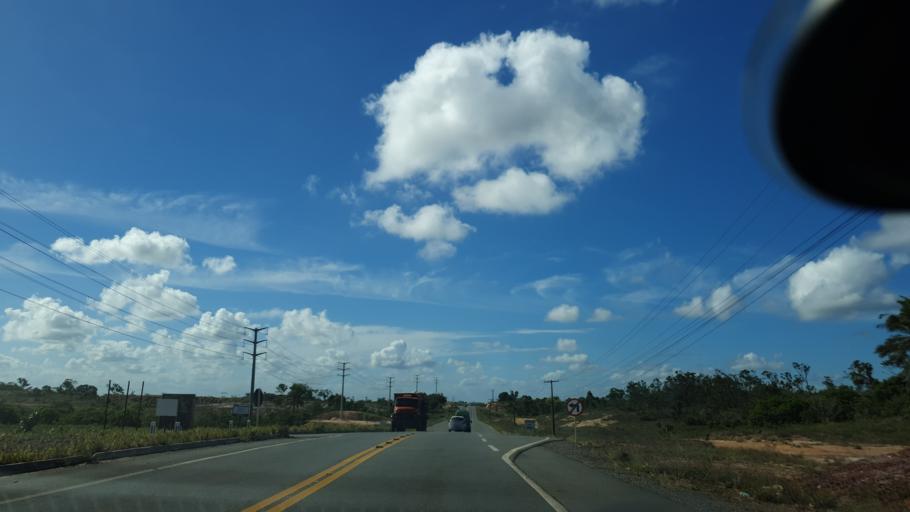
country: BR
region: Bahia
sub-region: Camacari
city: Camacari
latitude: -12.6980
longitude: -38.2193
